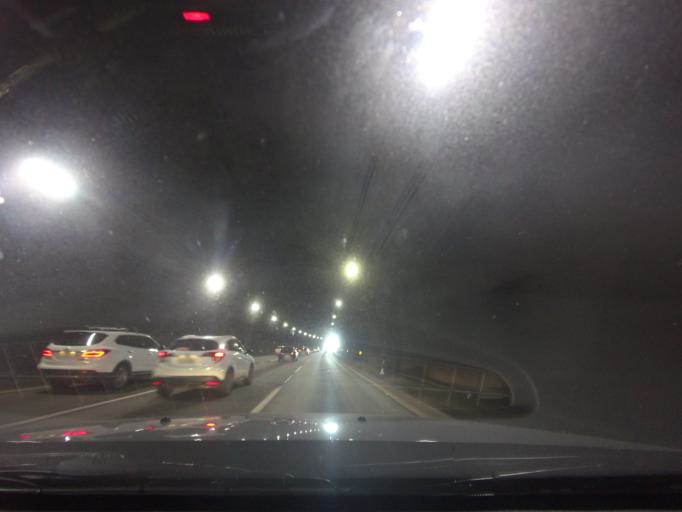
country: BR
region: Sao Paulo
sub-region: Cubatao
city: Cubatao
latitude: -23.9132
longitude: -46.5199
